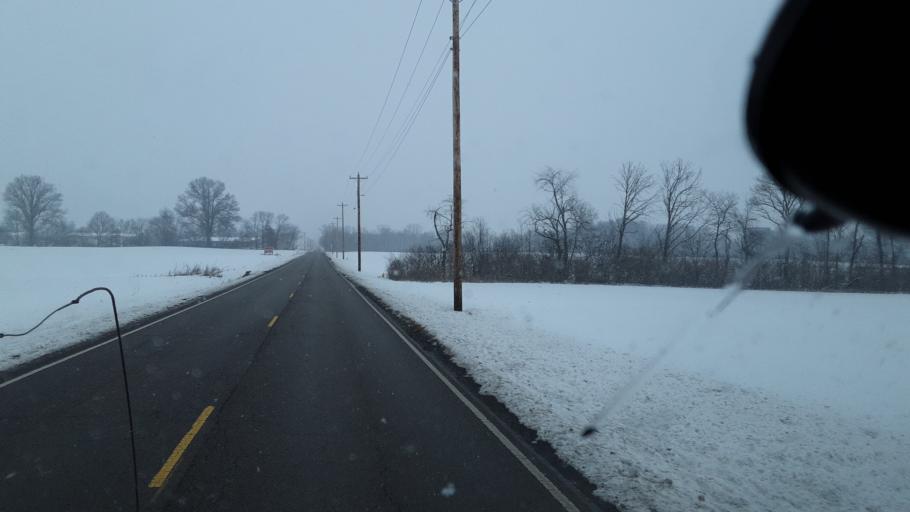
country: US
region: Ohio
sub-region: Licking County
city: Hebron
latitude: 40.0018
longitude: -82.4819
